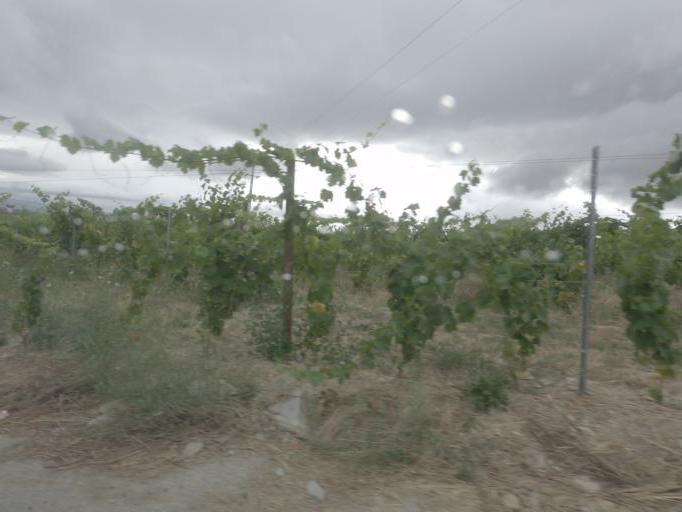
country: PT
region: Vila Real
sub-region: Sabrosa
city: Sabrosa
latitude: 41.2468
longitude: -7.4987
